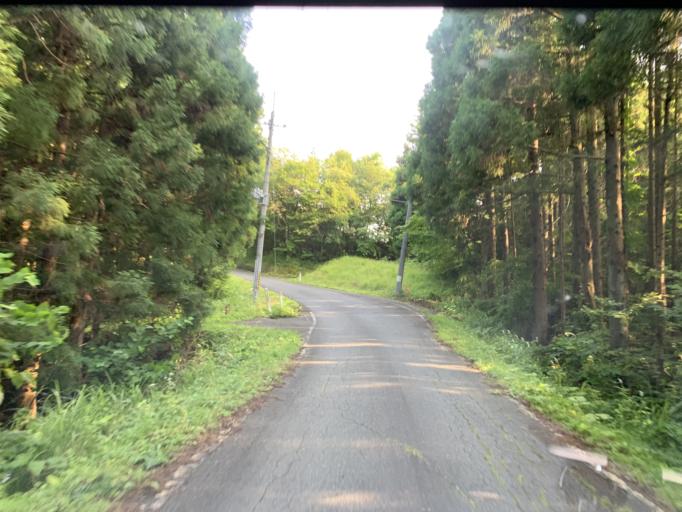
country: JP
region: Iwate
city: Ichinoseki
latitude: 38.8363
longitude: 141.1500
